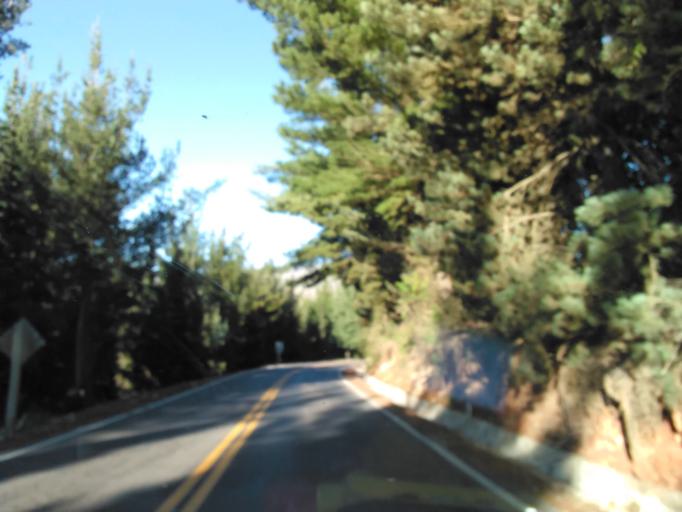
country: BO
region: Cochabamba
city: Mizque
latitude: -17.8391
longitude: -65.4439
